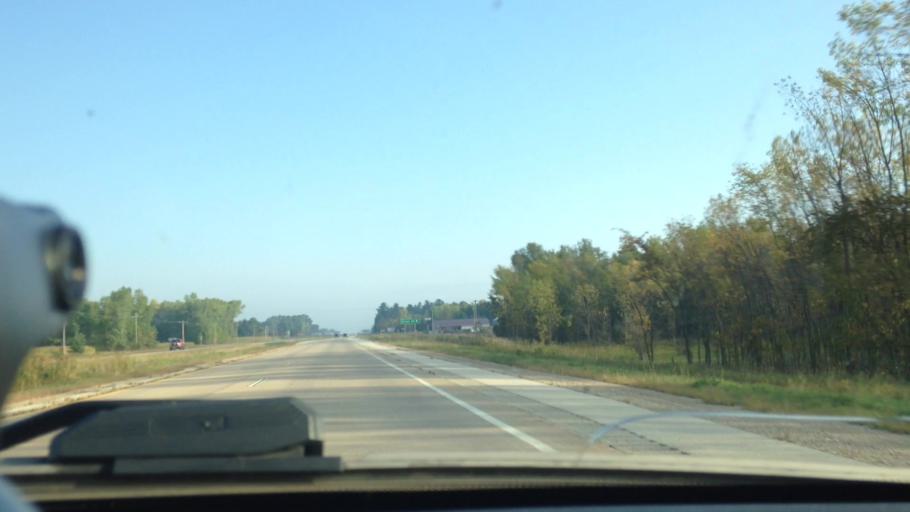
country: US
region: Wisconsin
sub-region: Oconto County
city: Oconto Falls
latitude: 45.0194
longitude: -88.0449
